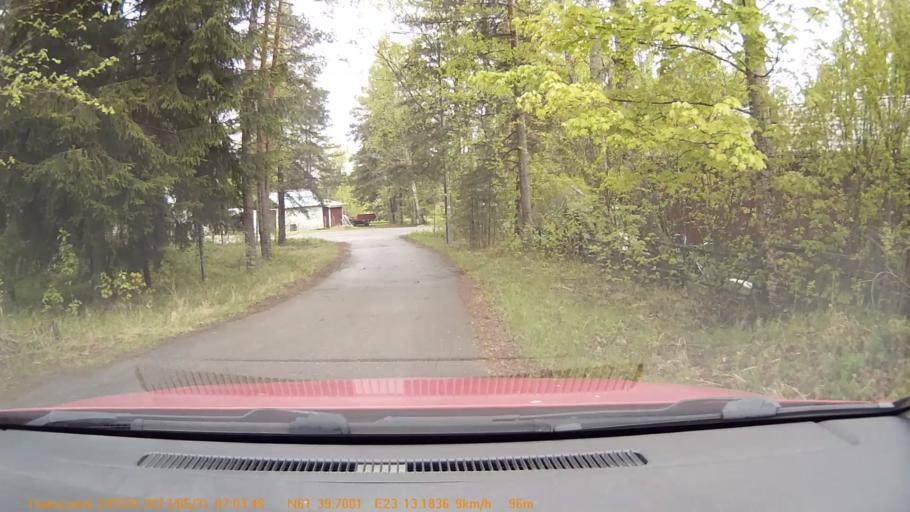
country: FI
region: Pirkanmaa
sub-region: Tampere
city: Haemeenkyroe
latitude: 61.6617
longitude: 23.2197
